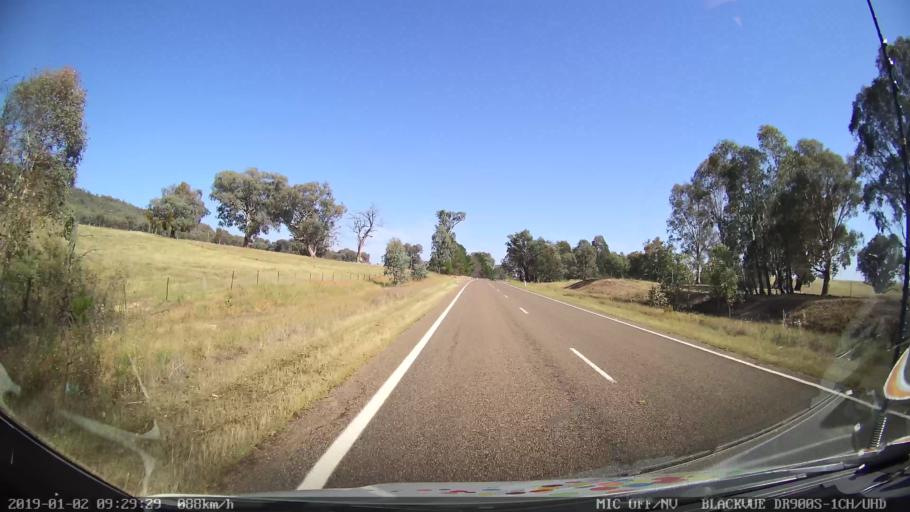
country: AU
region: New South Wales
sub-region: Tumut Shire
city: Tumut
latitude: -35.3381
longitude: 148.2420
